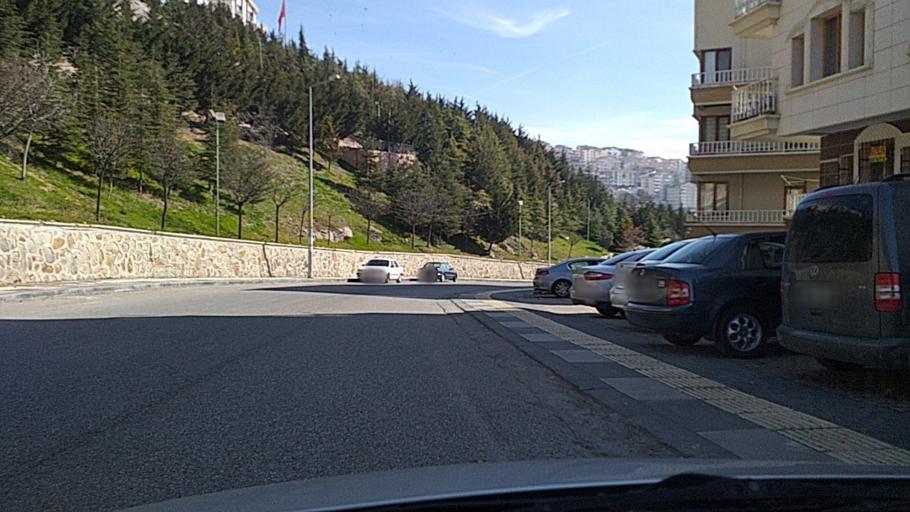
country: TR
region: Ankara
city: Ankara
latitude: 39.9895
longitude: 32.8149
